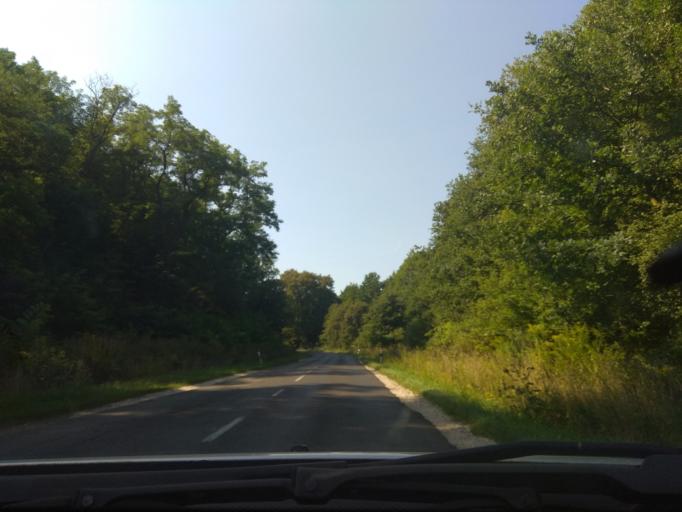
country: HU
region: Borsod-Abauj-Zemplen
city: Harsany
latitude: 47.9951
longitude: 20.7541
